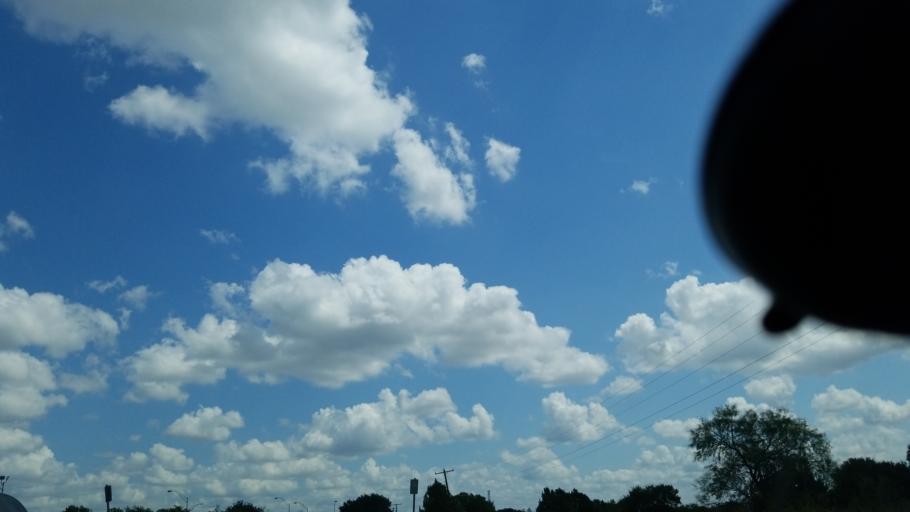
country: US
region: Texas
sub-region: Dallas County
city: Grand Prairie
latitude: 32.7047
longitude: -96.9849
